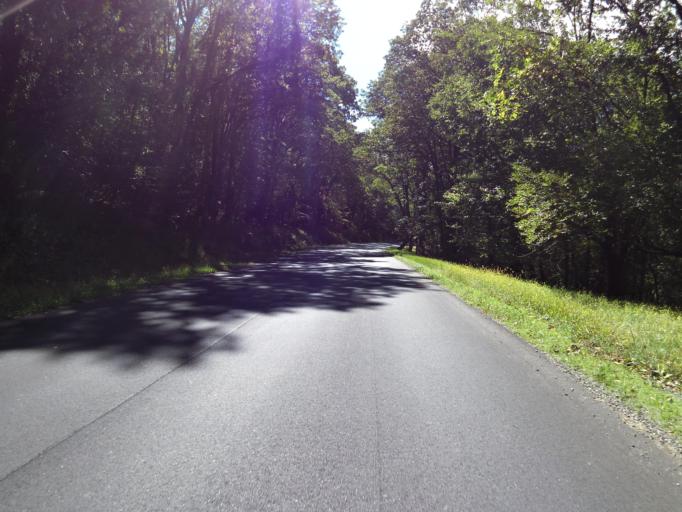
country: US
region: Virginia
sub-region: Page County
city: Luray
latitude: 38.6783
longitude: -78.3305
